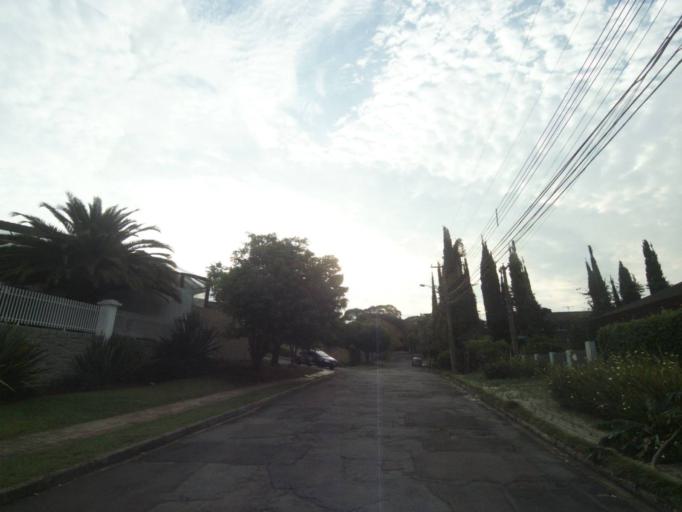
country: BR
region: Parana
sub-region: Curitiba
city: Curitiba
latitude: -25.3998
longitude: -49.2809
